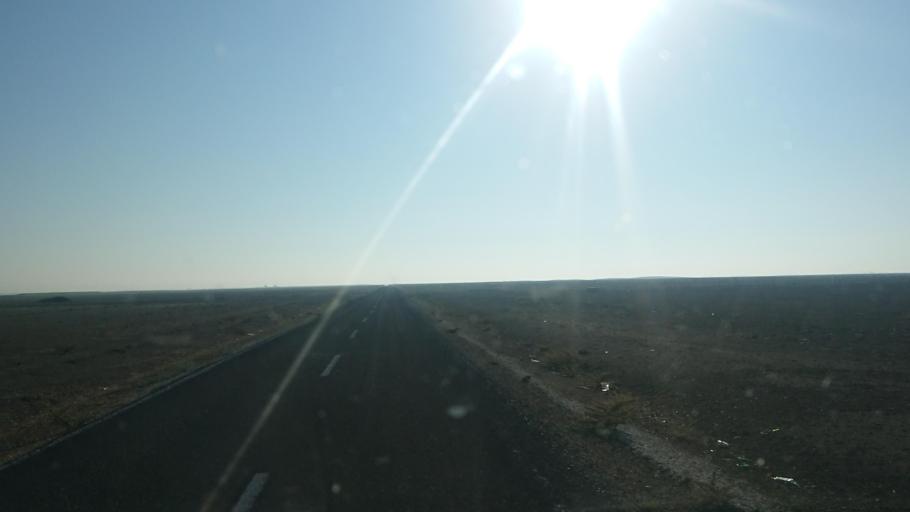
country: TR
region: Aksaray
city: Yesilova
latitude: 38.3879
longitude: 33.7560
